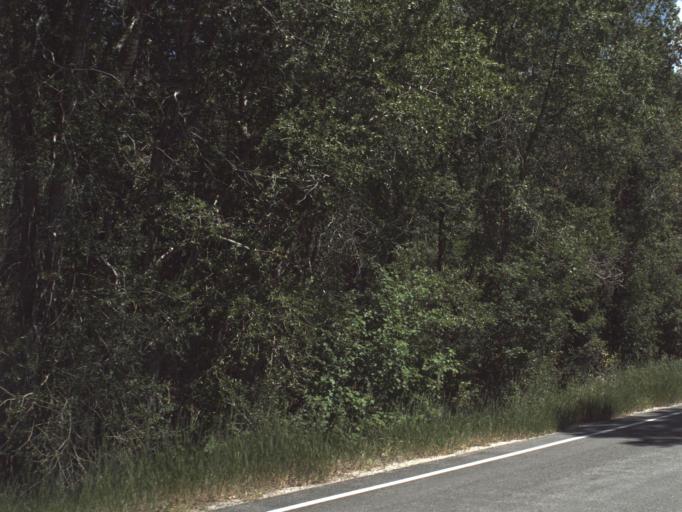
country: US
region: Utah
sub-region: Weber County
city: Wolf Creek
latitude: 41.3553
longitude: -111.5957
